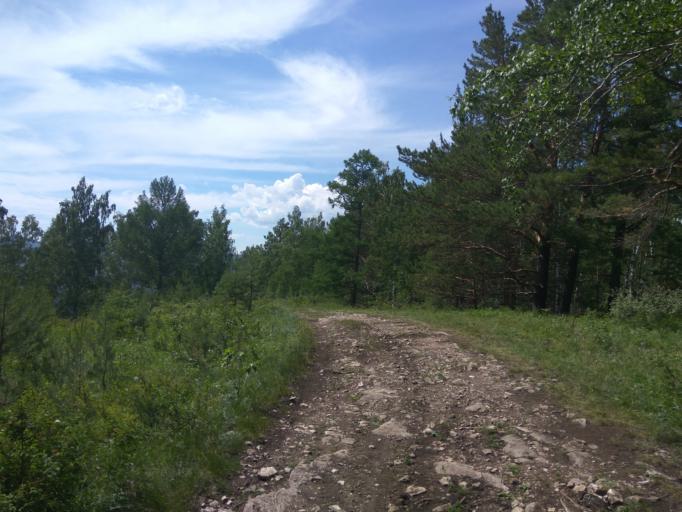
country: RU
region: Krasnoyarskiy
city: Krasnoyarsk
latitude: 55.9464
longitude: 92.8680
